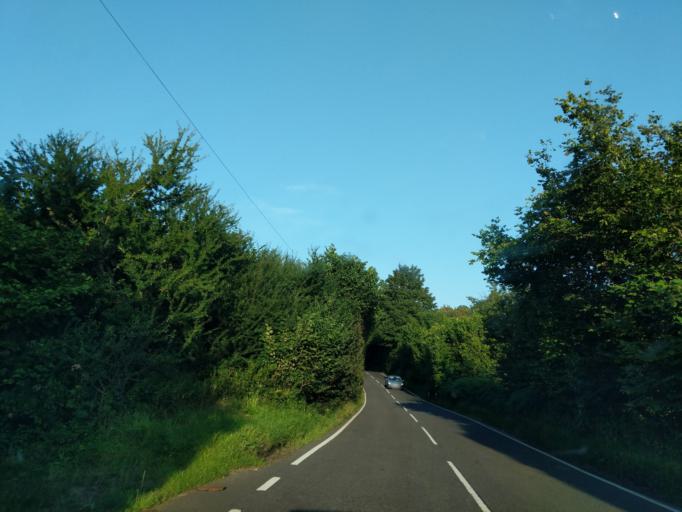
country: GB
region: Scotland
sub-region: Stirling
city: Balfron
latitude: 56.1780
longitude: -4.3190
